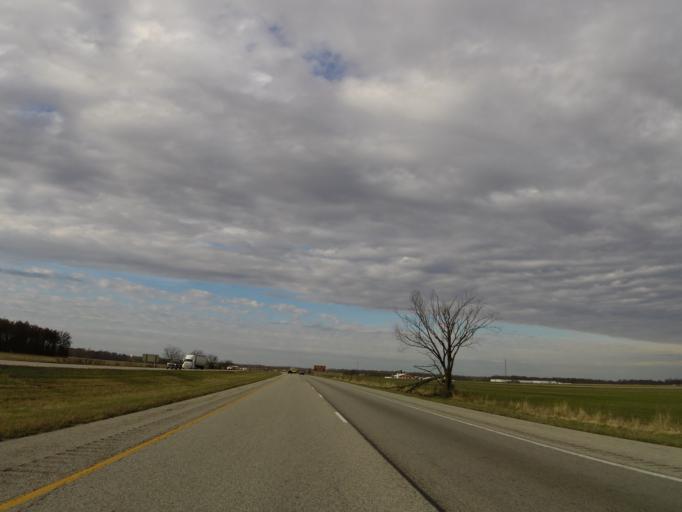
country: US
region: Illinois
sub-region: Washington County
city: Nashville
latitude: 38.3915
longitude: -89.3499
